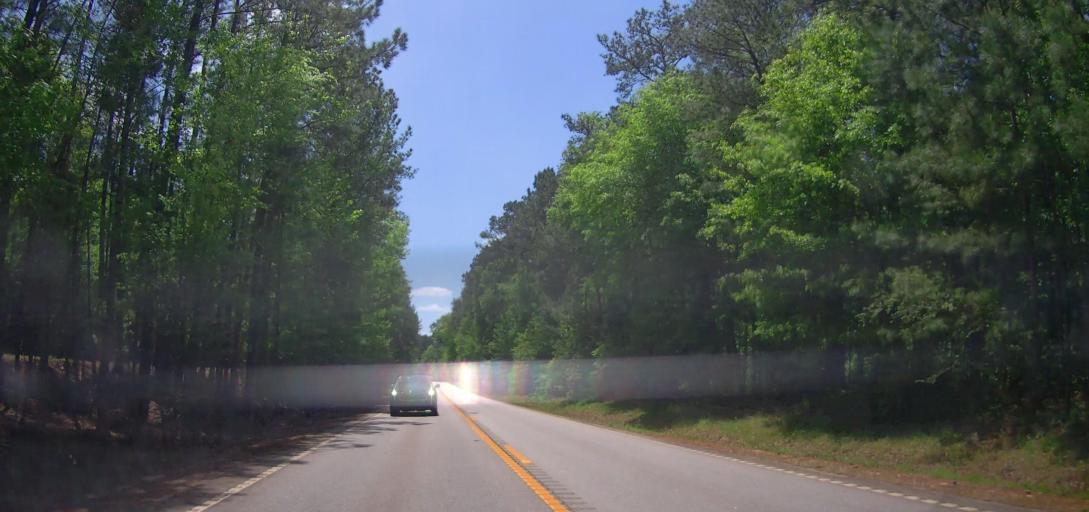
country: US
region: Georgia
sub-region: Jasper County
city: Monticello
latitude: 33.2670
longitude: -83.6752
